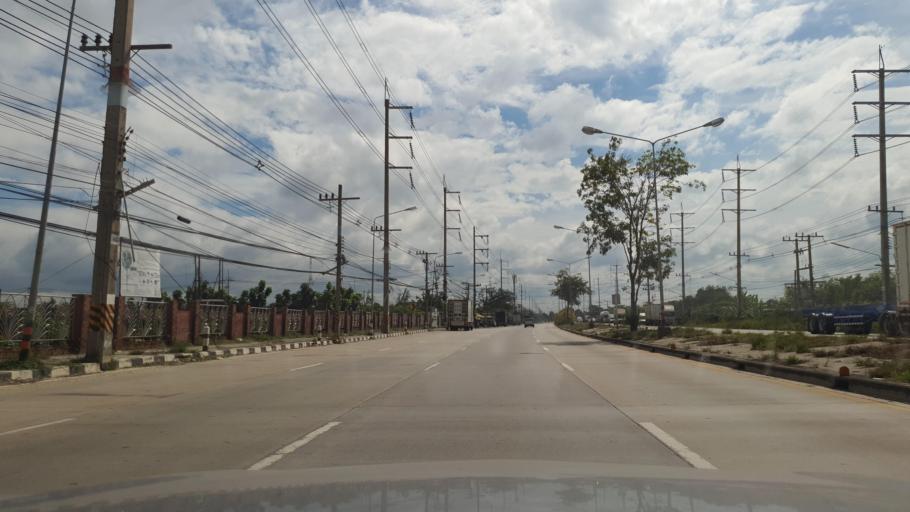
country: TH
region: Chachoengsao
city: Bang Pakong
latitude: 13.5317
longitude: 100.9924
